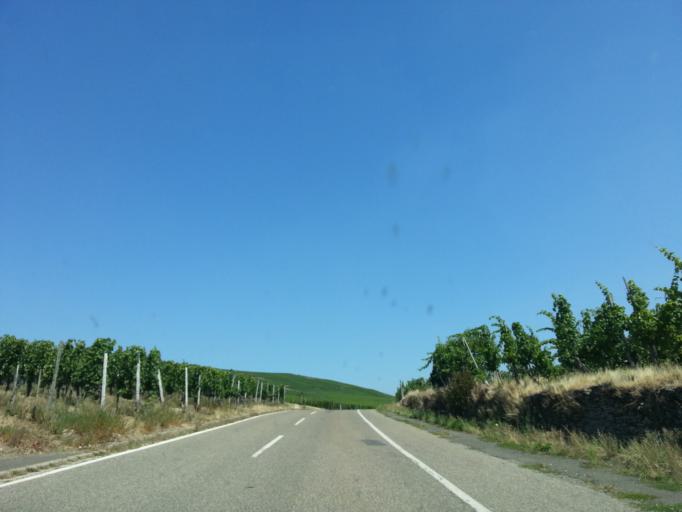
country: DE
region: Rheinland-Pfalz
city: Minheim
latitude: 49.8691
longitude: 6.9380
